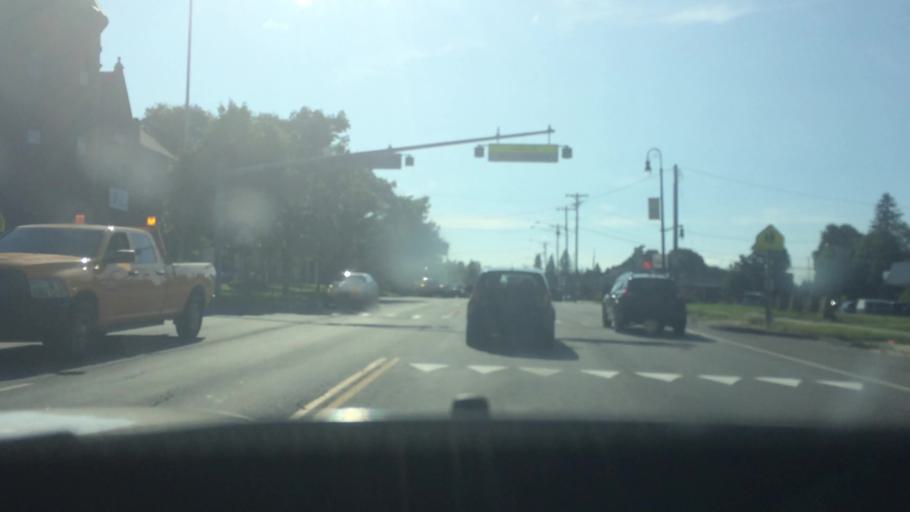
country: US
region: New York
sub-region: Franklin County
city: Malone
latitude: 44.8488
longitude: -74.2972
